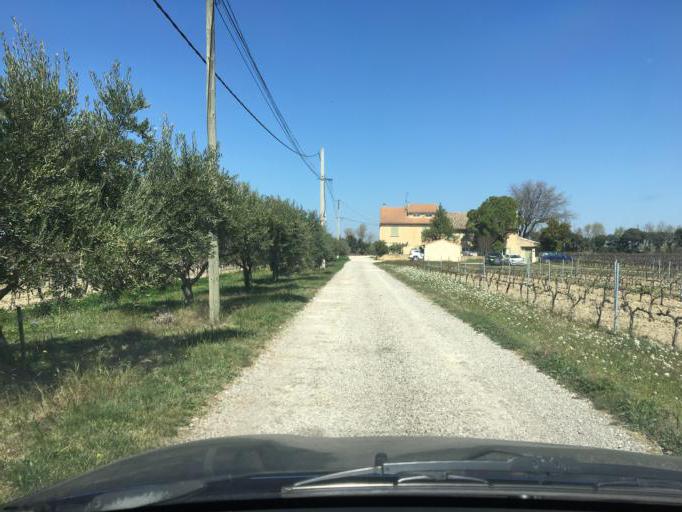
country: FR
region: Provence-Alpes-Cote d'Azur
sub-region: Departement du Vaucluse
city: Serignan-du-Comtat
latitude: 44.1742
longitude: 4.8456
